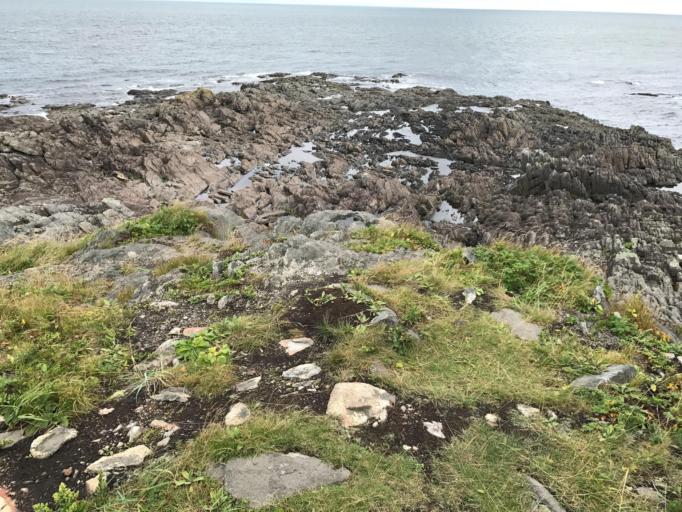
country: JP
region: Hokkaido
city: Mombetsu
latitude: 44.5314
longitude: 143.0619
